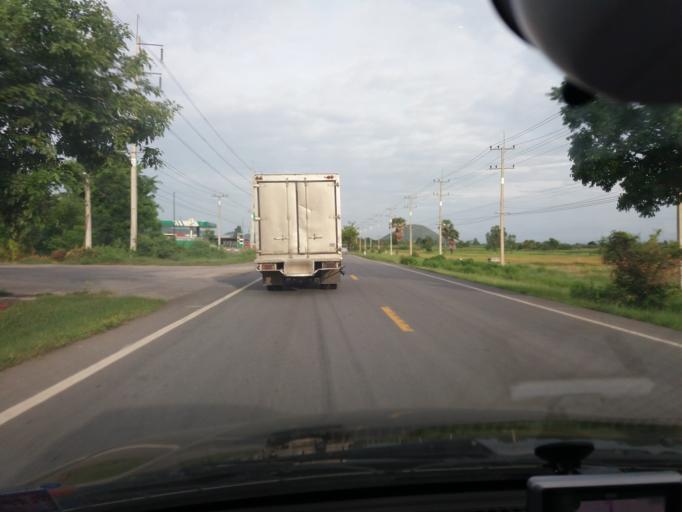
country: TH
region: Kanchanaburi
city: Huai Krachao
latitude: 14.3321
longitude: 99.7345
